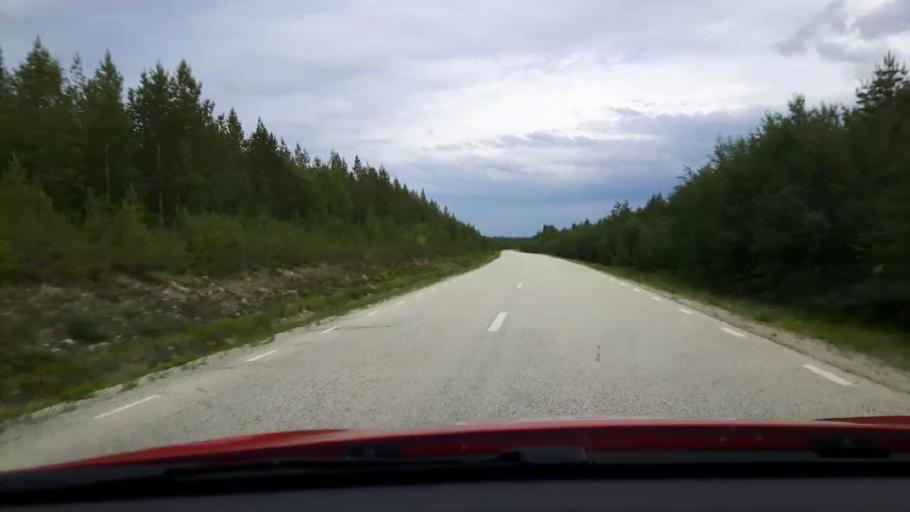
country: SE
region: Jaemtland
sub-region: Bergs Kommun
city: Hoverberg
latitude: 62.6974
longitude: 13.9631
